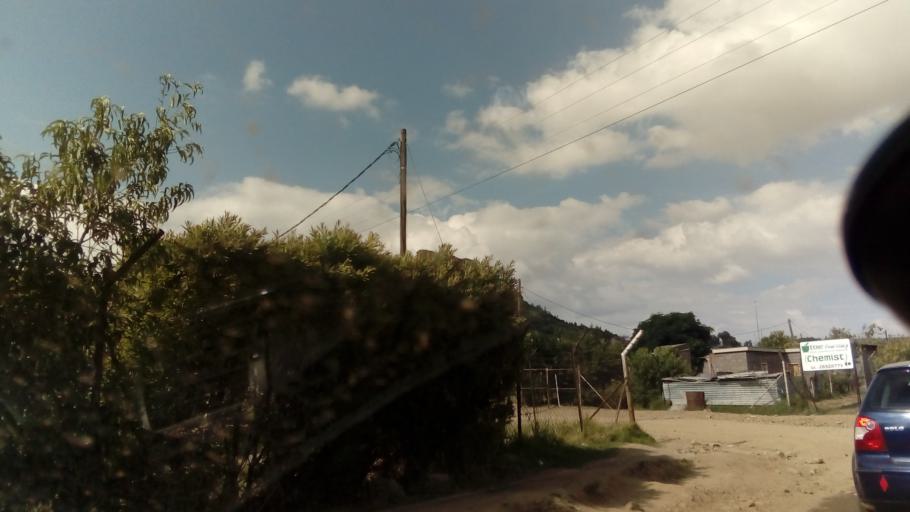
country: LS
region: Maseru
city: Maseru
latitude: -29.3706
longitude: 27.5341
